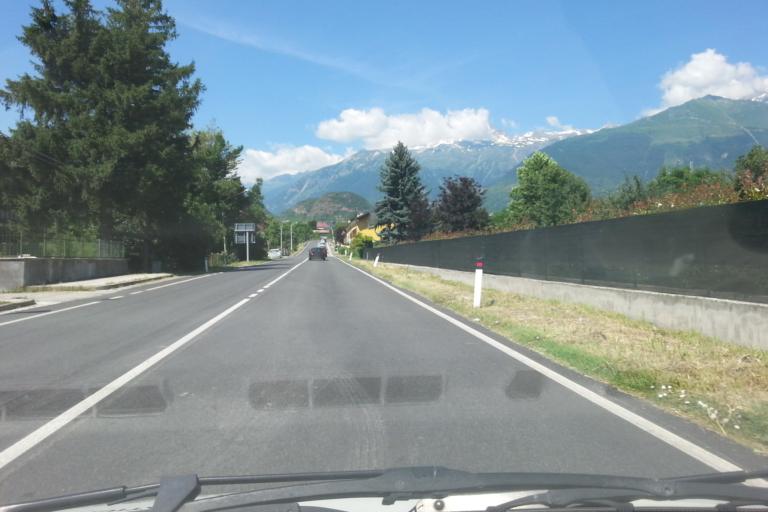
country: IT
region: Piedmont
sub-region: Provincia di Torino
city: Susa
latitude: 45.1370
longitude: 7.0702
